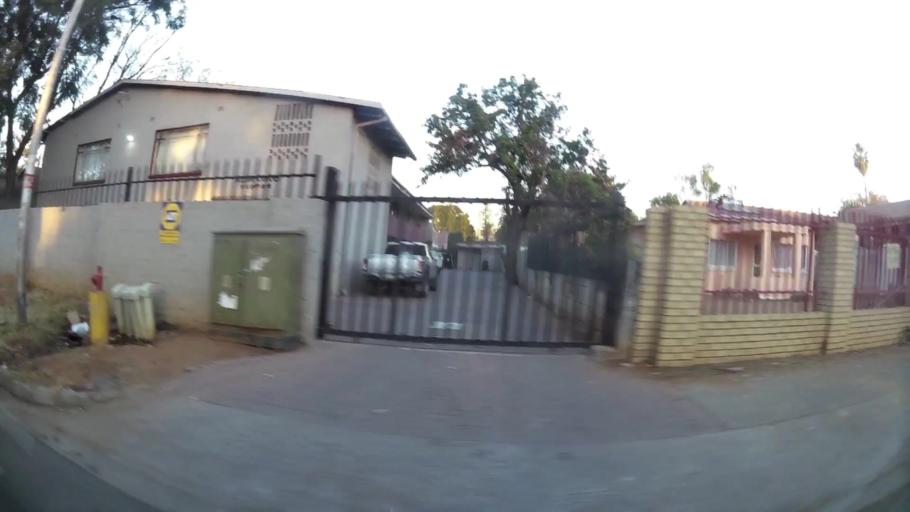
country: ZA
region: North-West
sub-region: Bojanala Platinum District Municipality
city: Rustenburg
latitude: -25.6655
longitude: 27.2461
